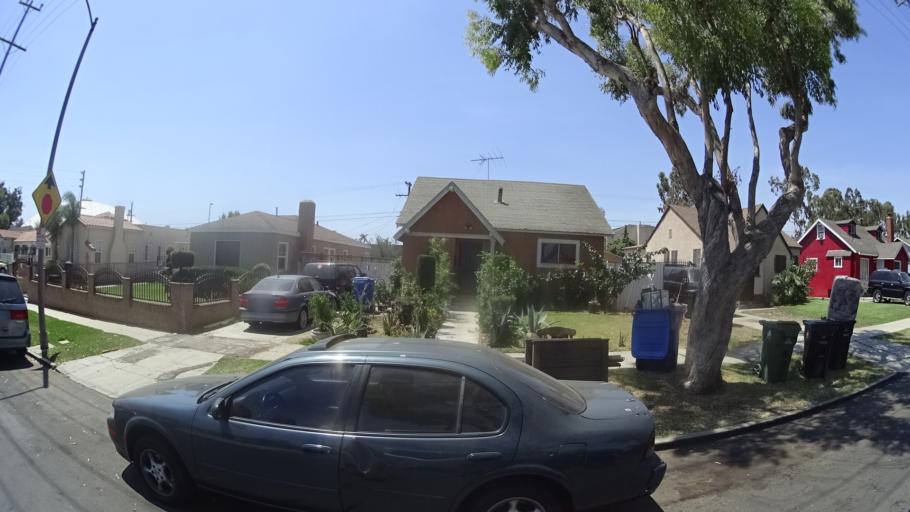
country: US
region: California
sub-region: Los Angeles County
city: Westmont
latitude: 33.9694
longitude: -118.2990
